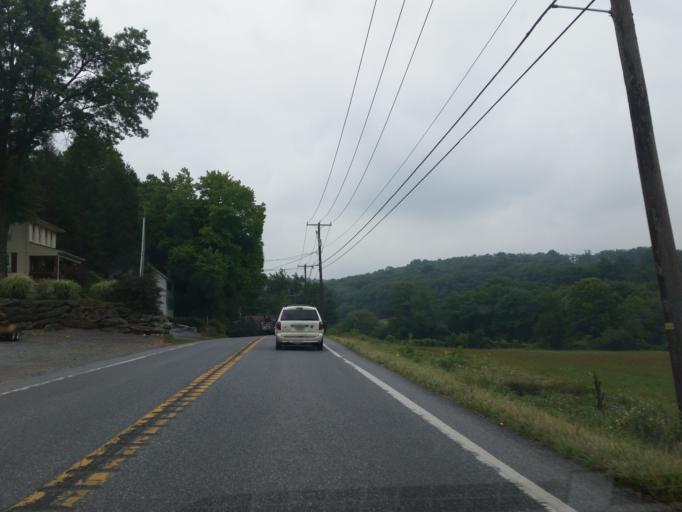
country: US
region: Pennsylvania
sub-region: Lancaster County
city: Brickerville
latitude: 40.2600
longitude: -76.3074
